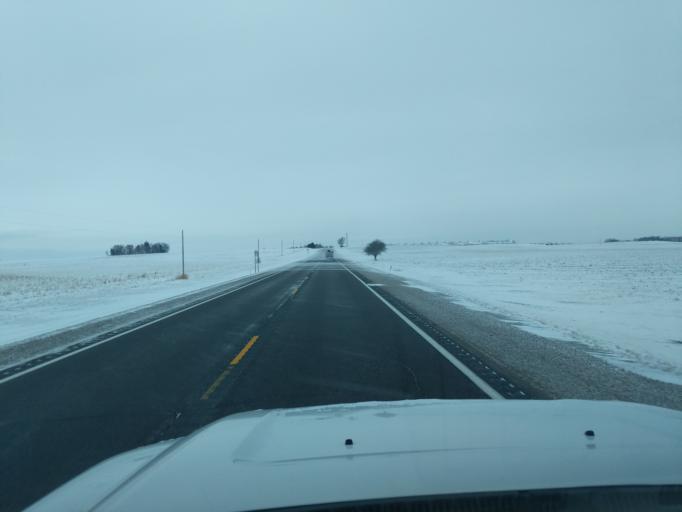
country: US
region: Minnesota
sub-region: Redwood County
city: Redwood Falls
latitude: 44.6132
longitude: -94.9946
